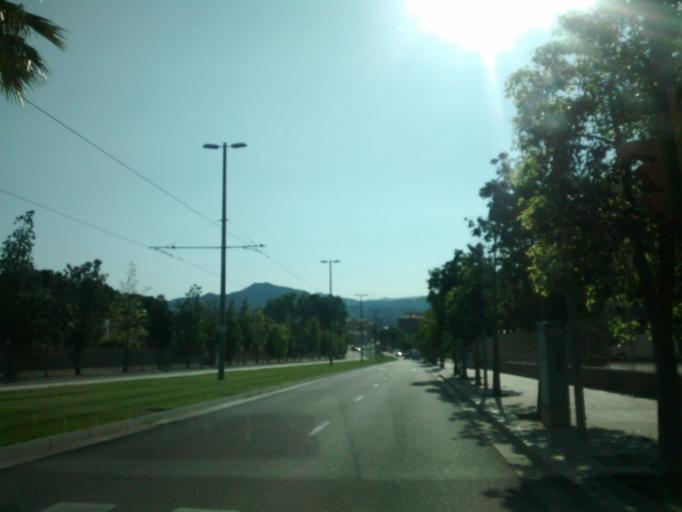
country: ES
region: Catalonia
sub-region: Provincia de Barcelona
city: Sant Feliu de Llobregat
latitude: 41.3798
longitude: 2.0582
